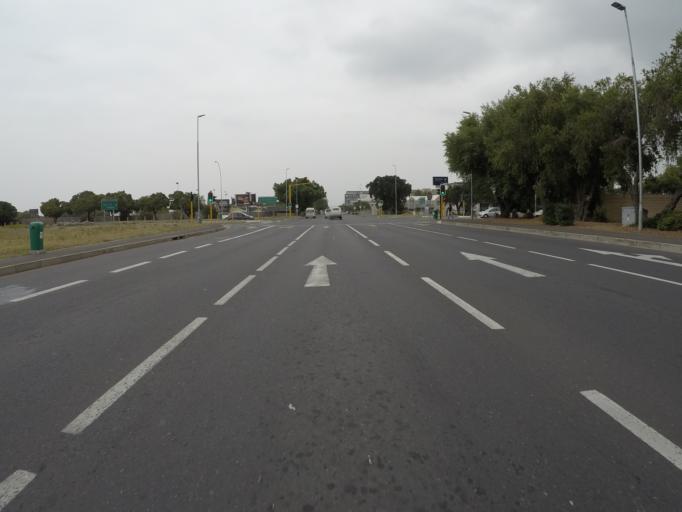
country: ZA
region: Western Cape
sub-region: City of Cape Town
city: Kraaifontein
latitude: -33.8767
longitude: 18.6375
